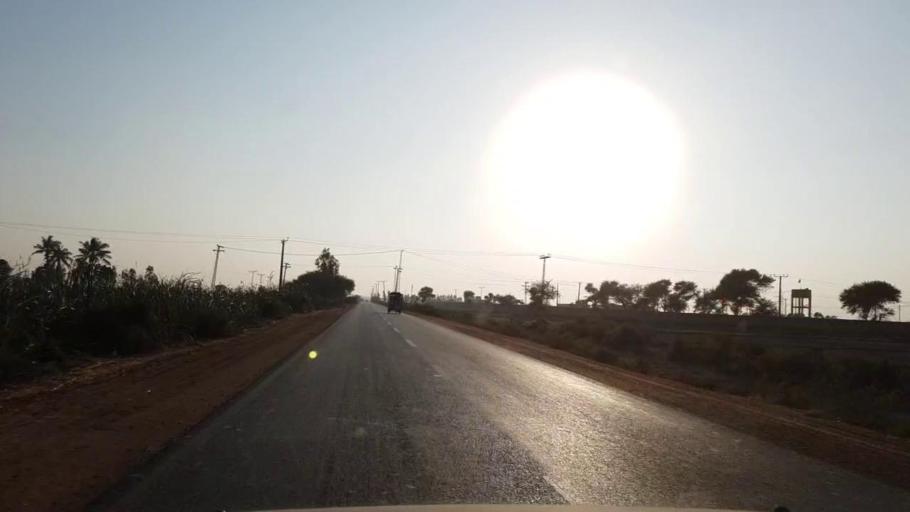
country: PK
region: Sindh
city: Daro Mehar
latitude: 24.6277
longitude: 68.1016
